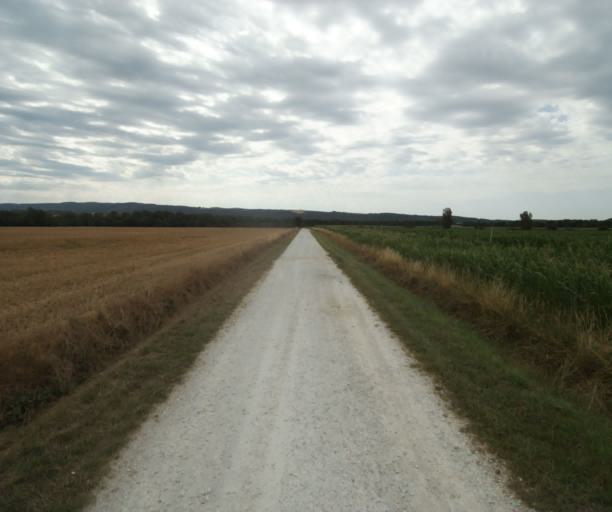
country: FR
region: Midi-Pyrenees
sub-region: Departement de la Haute-Garonne
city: Saint-Felix-Lauragais
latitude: 43.4359
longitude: 1.9451
